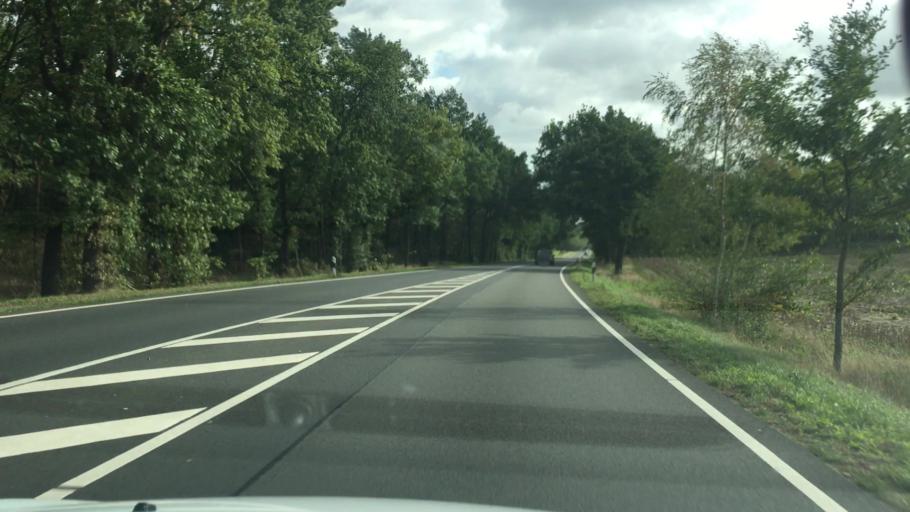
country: DE
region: Lower Saxony
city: Diepholz
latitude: 52.6446
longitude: 8.3433
